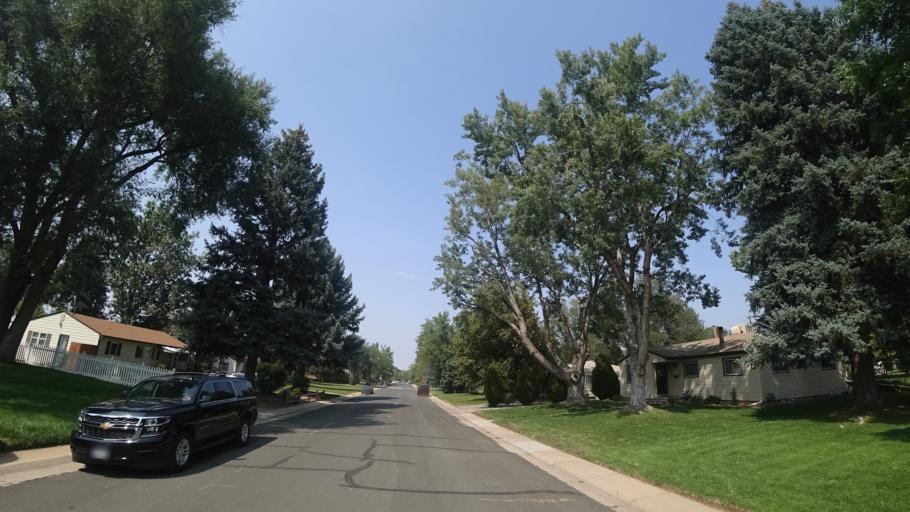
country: US
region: Colorado
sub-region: Arapahoe County
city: Englewood
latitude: 39.6302
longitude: -104.9996
